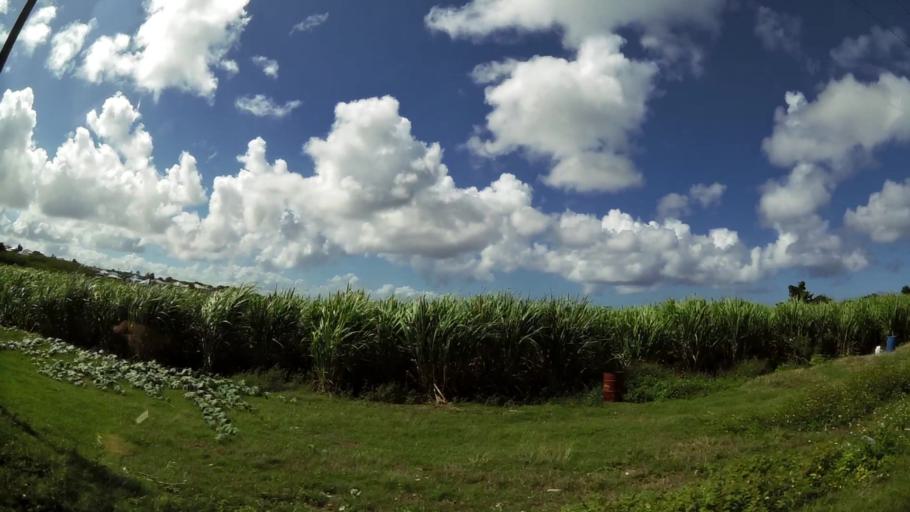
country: GP
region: Guadeloupe
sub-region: Guadeloupe
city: Anse-Bertrand
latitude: 16.4611
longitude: -61.4823
